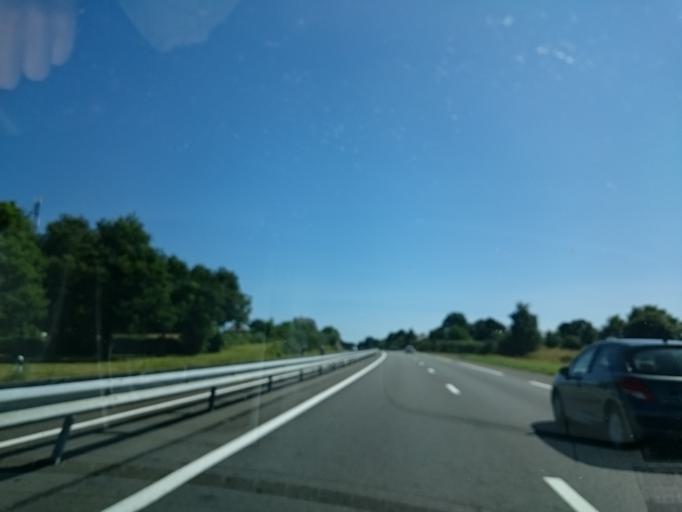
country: FR
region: Brittany
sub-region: Departement d'Ille-et-Vilaine
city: Saint-Pierre-de-Plesguen
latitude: 48.4465
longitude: -1.9247
